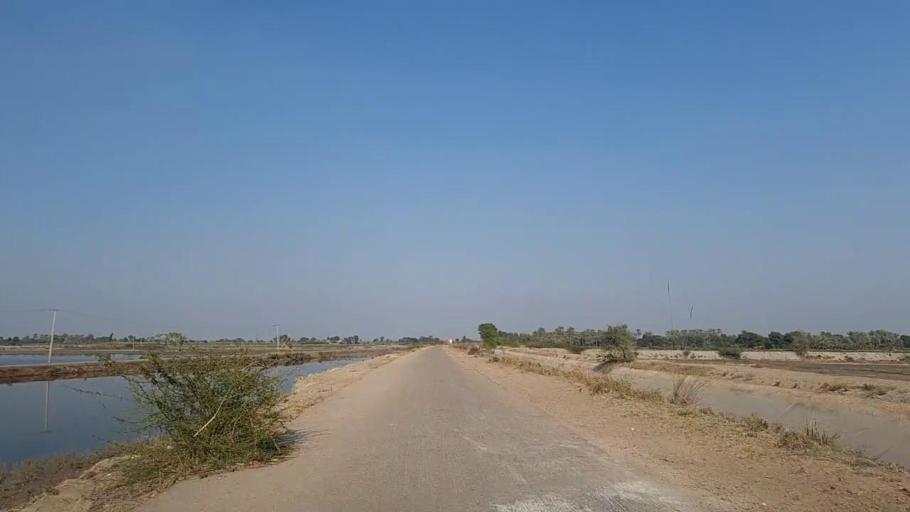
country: PK
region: Sindh
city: Daur
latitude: 26.4304
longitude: 68.2661
